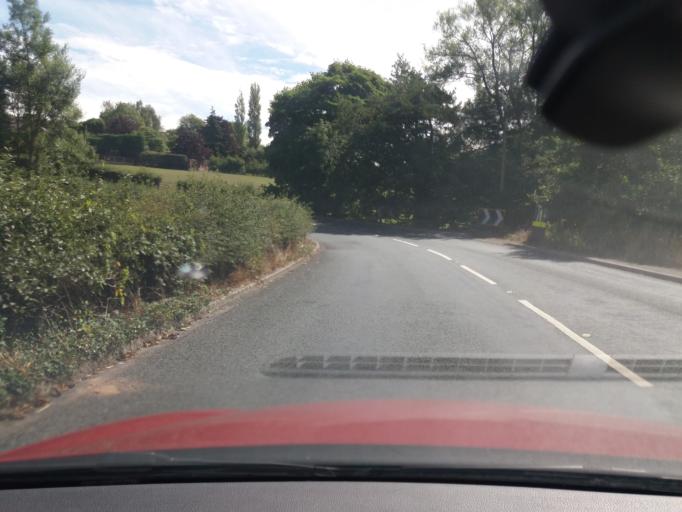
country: GB
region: England
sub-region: Lancashire
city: Euxton
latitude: 53.6618
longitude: -2.7074
